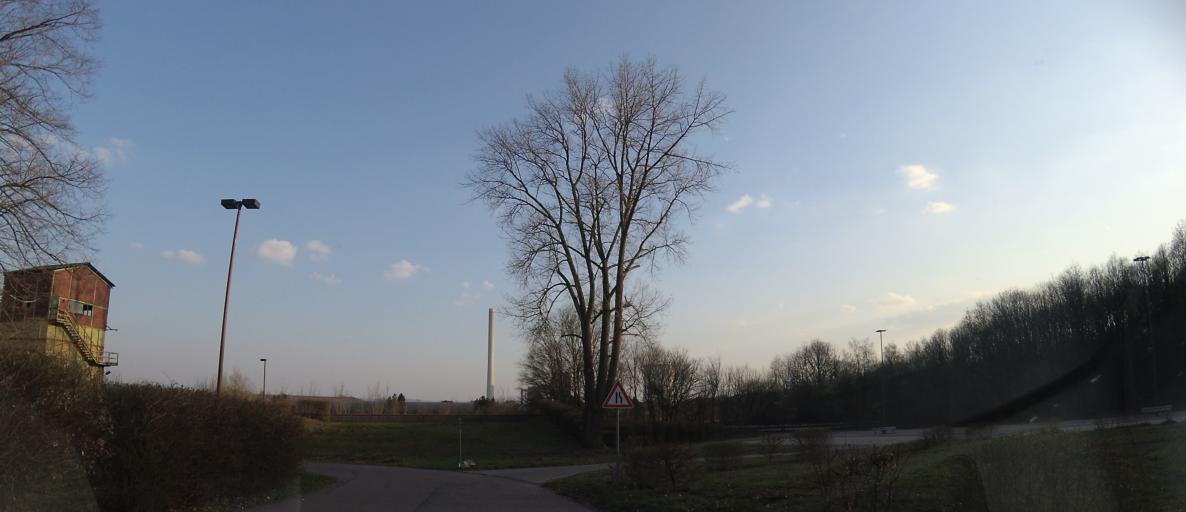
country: DE
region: Saarland
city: Merchweiler
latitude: 49.3432
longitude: 7.0327
